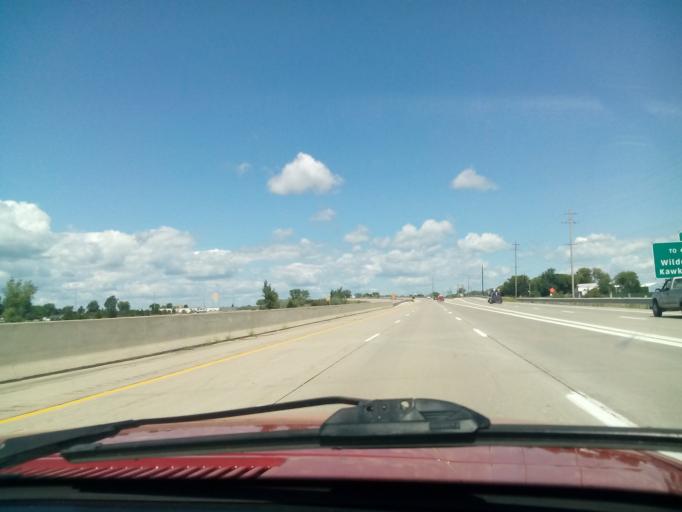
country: US
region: Michigan
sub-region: Bay County
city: Bay City
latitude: 43.6127
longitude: -83.9475
